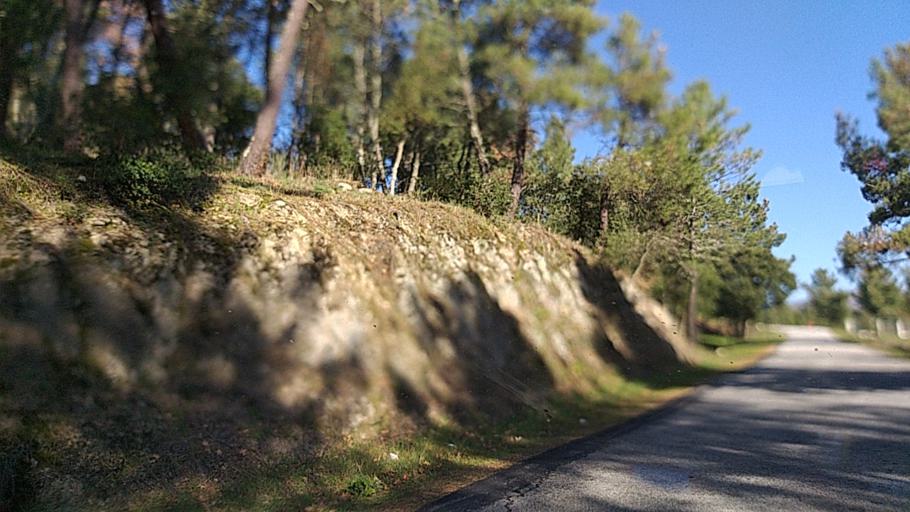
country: PT
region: Guarda
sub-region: Celorico da Beira
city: Celorico da Beira
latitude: 40.6933
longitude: -7.4535
